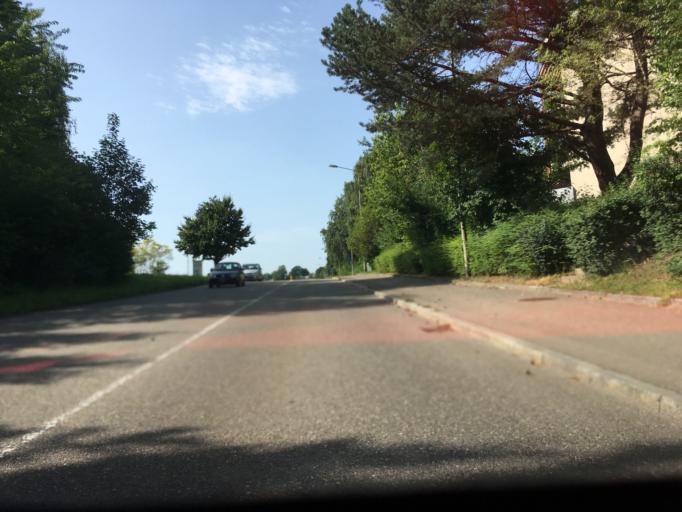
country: CH
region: Zurich
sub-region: Bezirk Buelach
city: Dietlikon / Dietlikon (Dorf)
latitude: 47.4163
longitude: 8.6161
